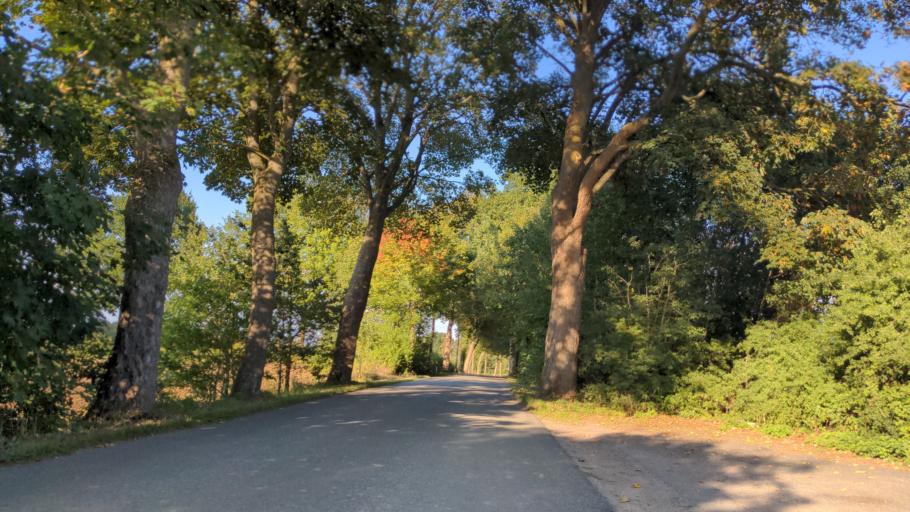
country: DE
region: Schleswig-Holstein
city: Ahrensbok
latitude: 53.9740
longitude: 10.6207
